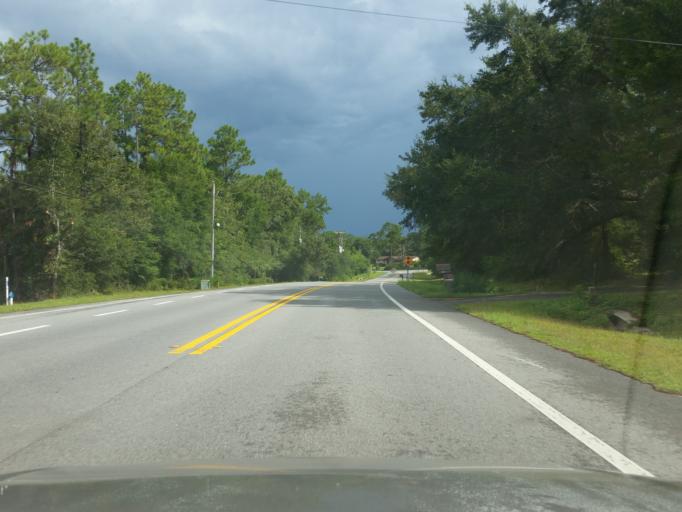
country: US
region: Florida
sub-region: Escambia County
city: Gonzalez
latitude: 30.5404
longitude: -87.3262
